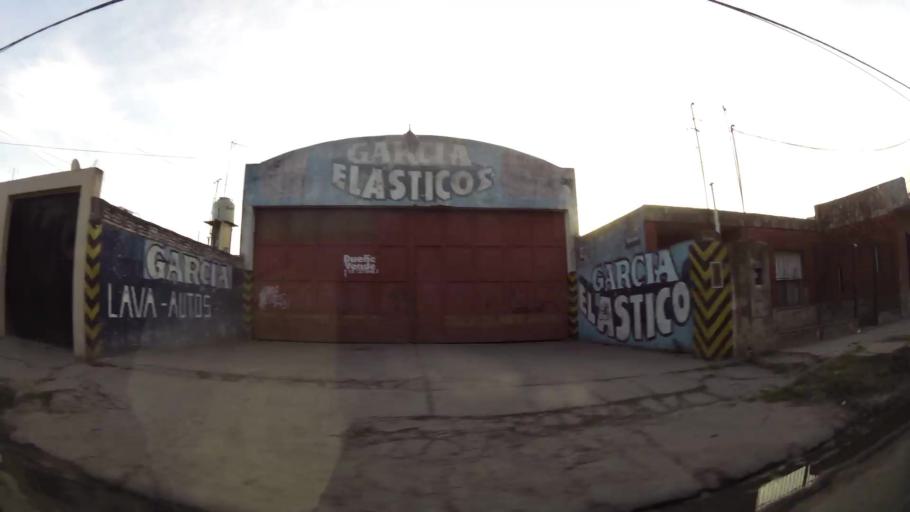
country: AR
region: Buenos Aires
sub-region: Partido de Almirante Brown
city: Adrogue
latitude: -34.7757
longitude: -58.3235
